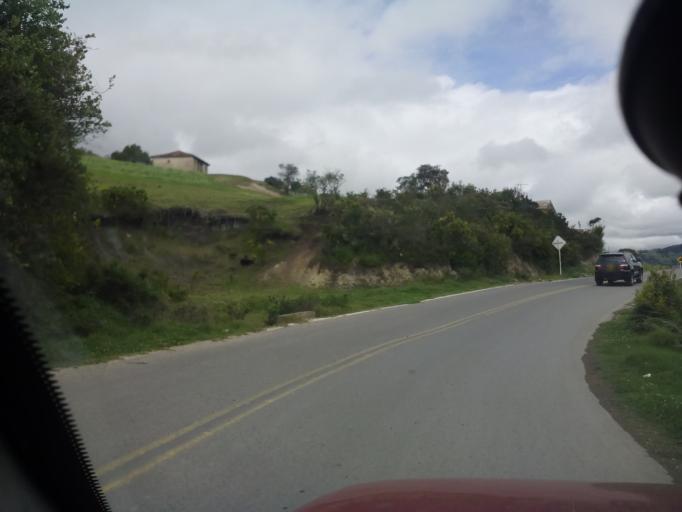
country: CO
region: Boyaca
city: Combita
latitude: 5.6360
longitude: -73.3456
